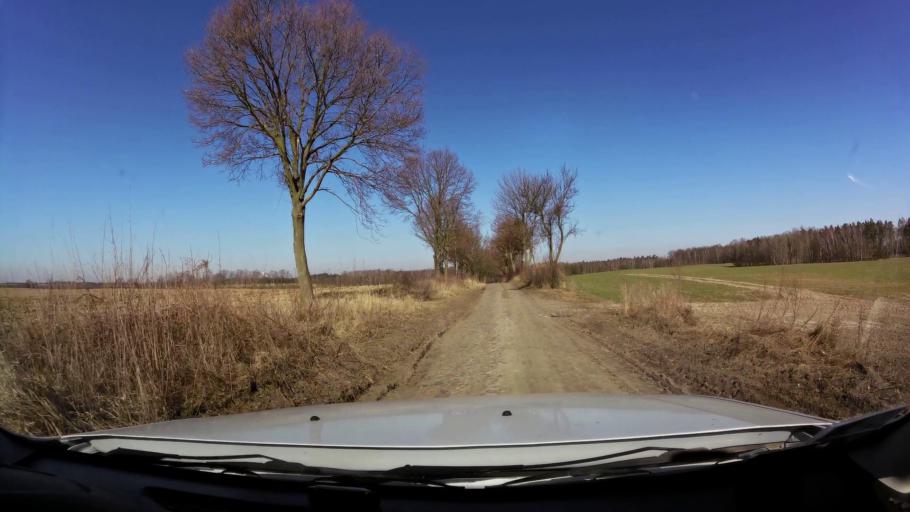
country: PL
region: West Pomeranian Voivodeship
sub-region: Powiat gryfinski
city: Banie
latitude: 53.1499
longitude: 14.6331
